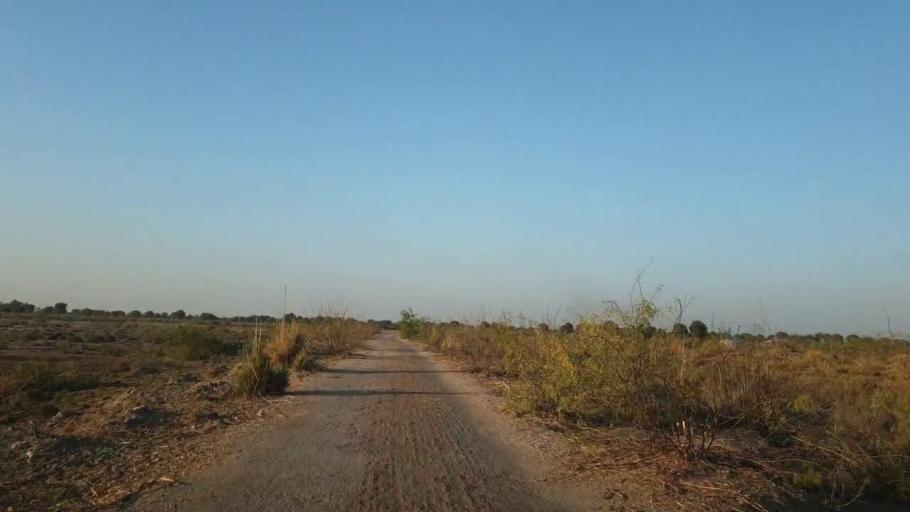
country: PK
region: Sindh
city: Mirpur Khas
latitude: 25.6853
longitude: 69.0504
